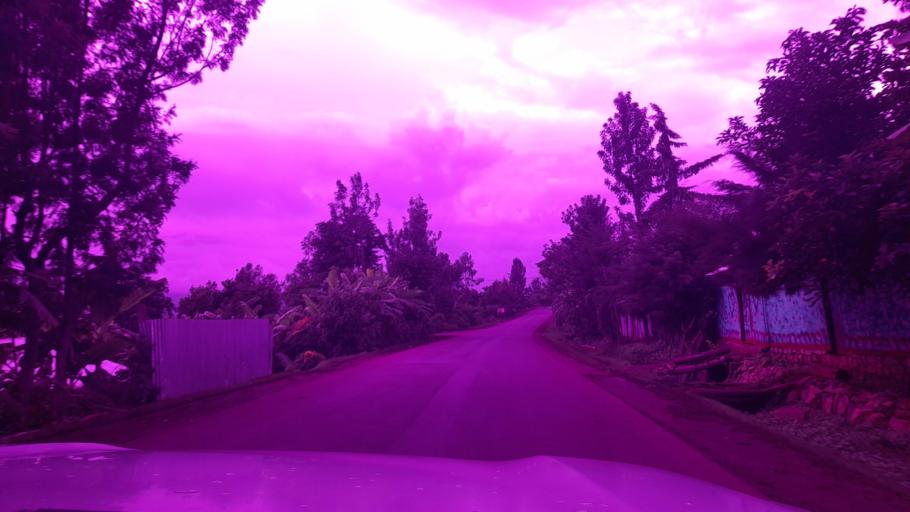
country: ET
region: Oromiya
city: Jima
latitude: 7.8970
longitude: 37.3892
